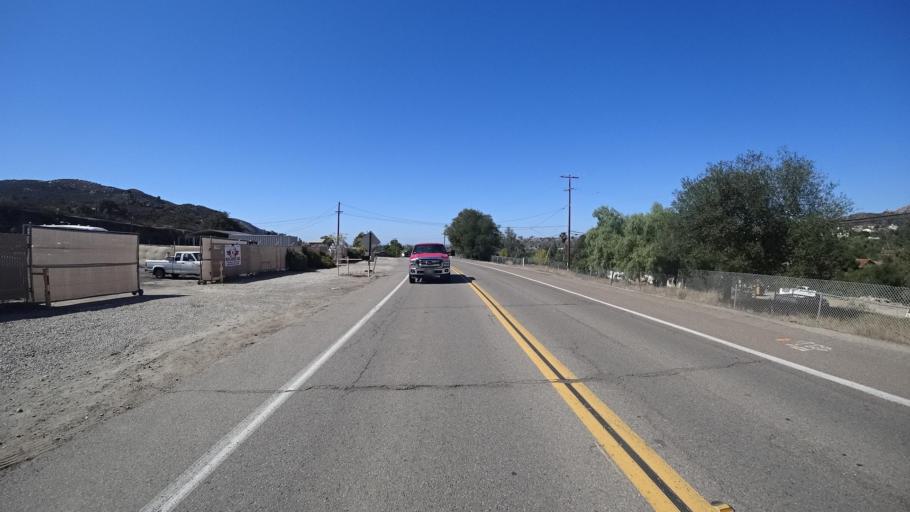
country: US
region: California
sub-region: San Diego County
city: Harbison Canyon
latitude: 32.8579
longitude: -116.8213
